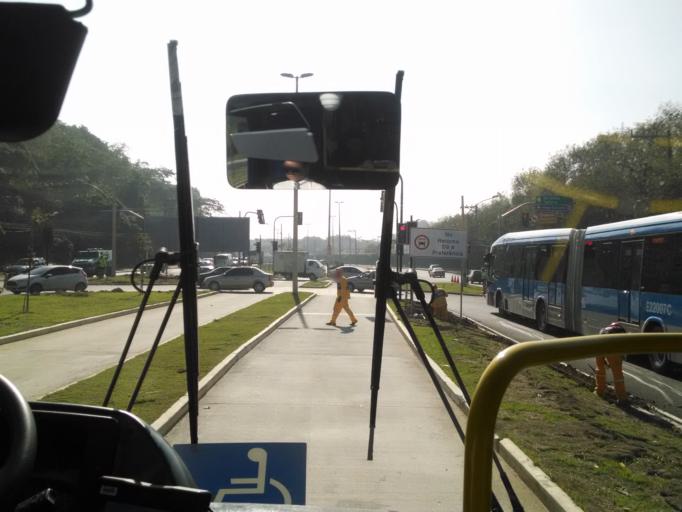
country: BR
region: Rio de Janeiro
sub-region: Sao Joao De Meriti
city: Sao Joao de Meriti
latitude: -22.9095
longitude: -43.3594
